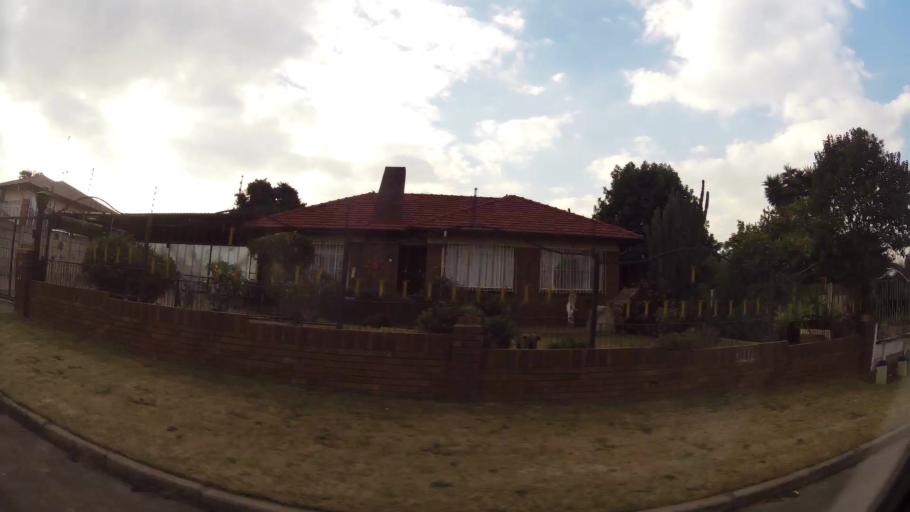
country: ZA
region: Gauteng
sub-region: Ekurhuleni Metropolitan Municipality
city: Germiston
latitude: -26.2458
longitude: 28.1956
